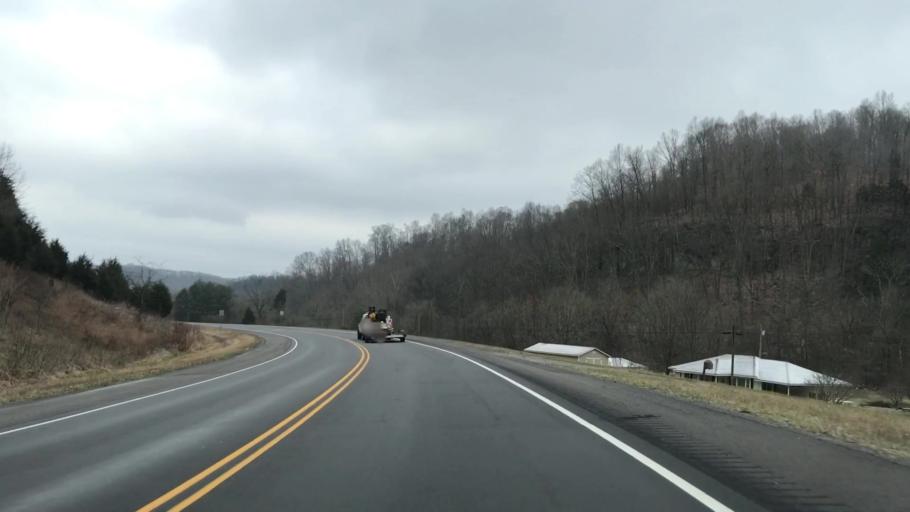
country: US
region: Kentucky
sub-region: Cumberland County
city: Burkesville
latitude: 36.8958
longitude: -85.4280
